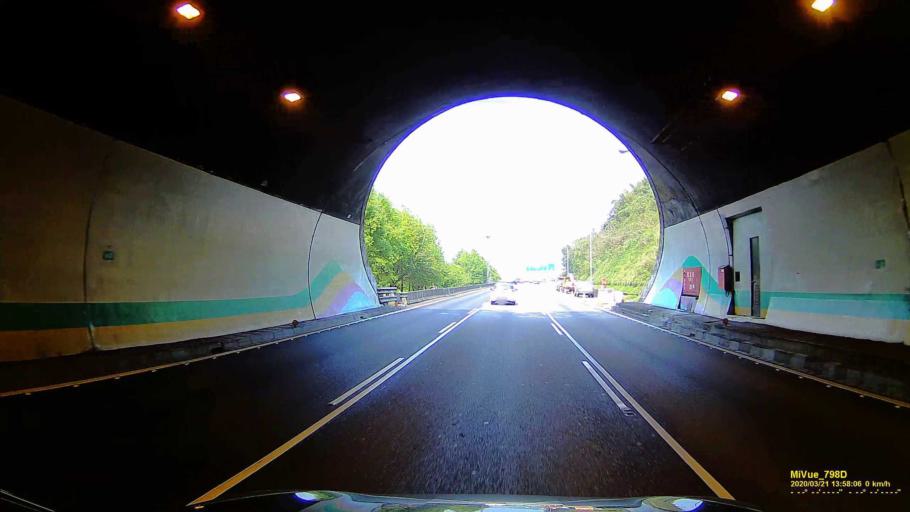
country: TW
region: Taipei
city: Taipei
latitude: 24.9682
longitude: 121.5493
